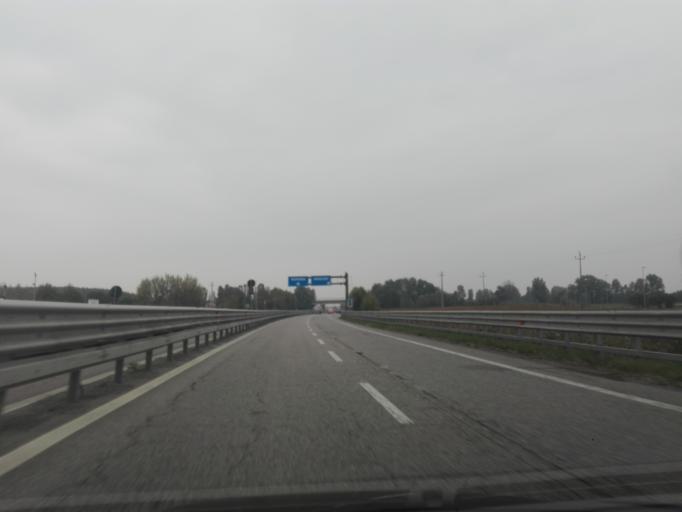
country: IT
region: Veneto
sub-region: Provincia di Verona
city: San Pietro di Morubio
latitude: 45.2262
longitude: 11.2368
